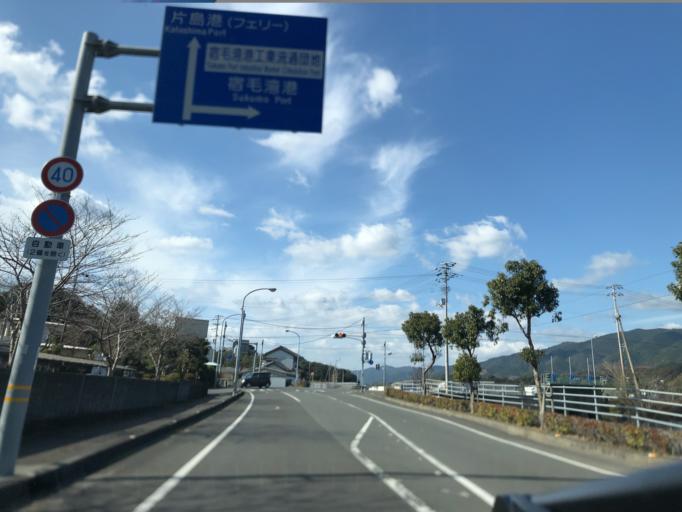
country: JP
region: Kochi
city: Sukumo
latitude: 32.9267
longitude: 132.6979
